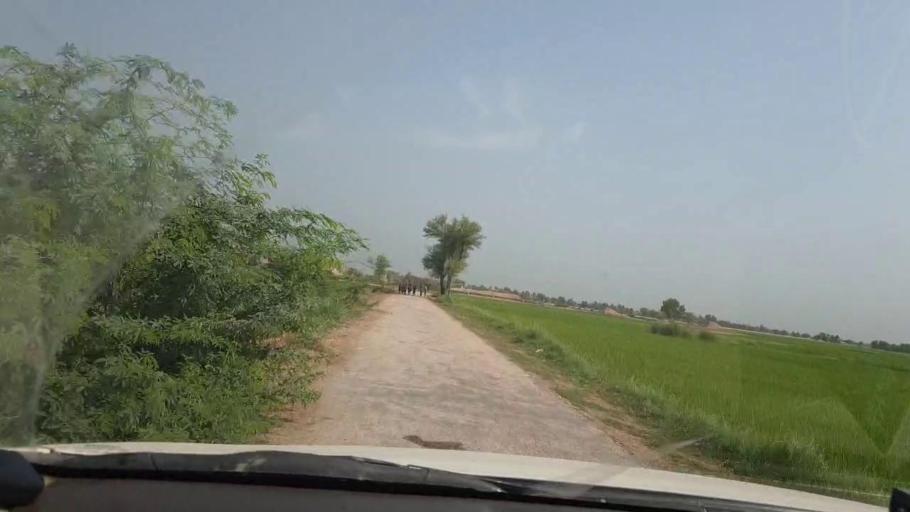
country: PK
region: Sindh
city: Chak
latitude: 27.8361
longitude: 68.7987
